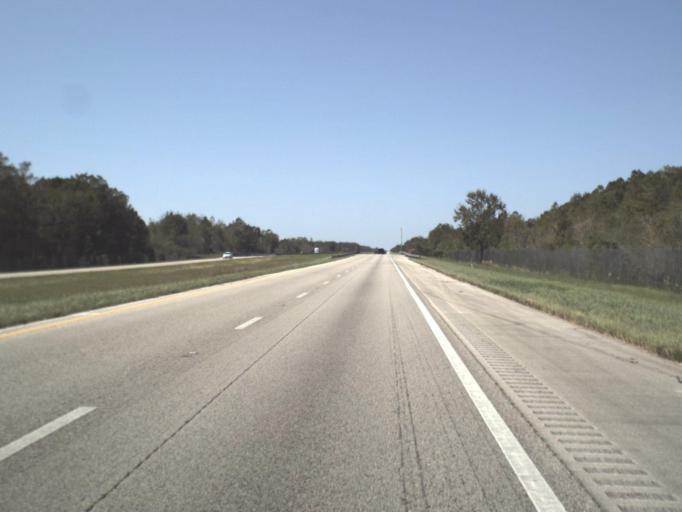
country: US
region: Florida
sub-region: Collier County
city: Orangetree
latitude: 26.1546
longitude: -81.3680
